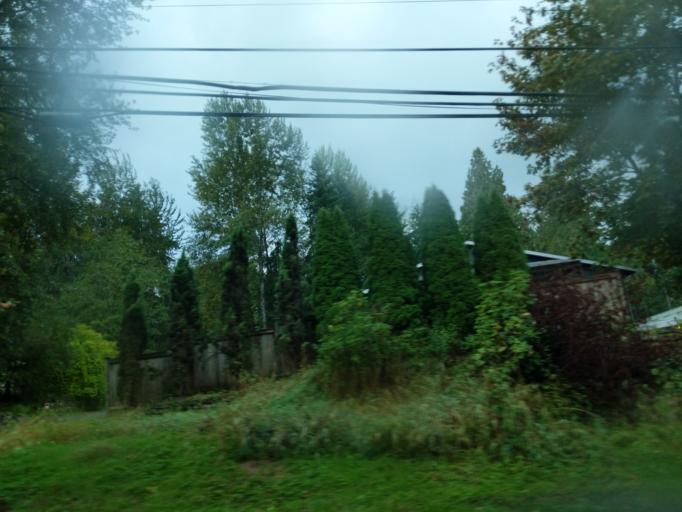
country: US
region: Washington
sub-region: King County
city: Bothell
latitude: 47.7889
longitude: -122.2077
